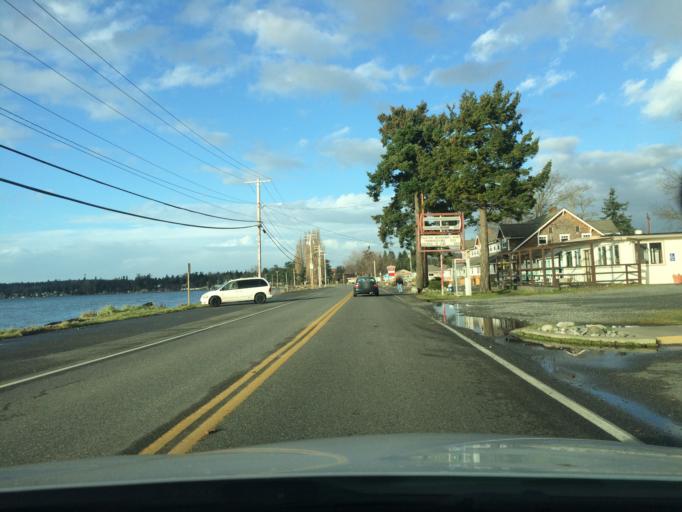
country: US
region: Washington
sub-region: Whatcom County
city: Birch Bay
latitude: 48.9271
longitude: -122.7452
